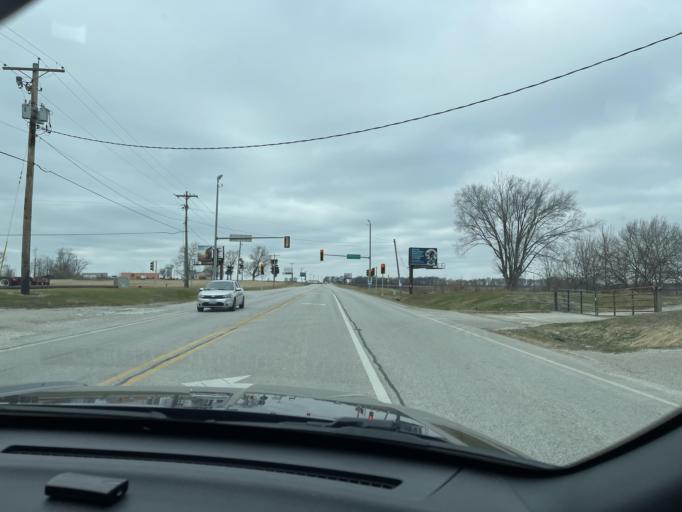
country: US
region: Illinois
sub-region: Sangamon County
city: Leland Grove
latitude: 39.8234
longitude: -89.7388
